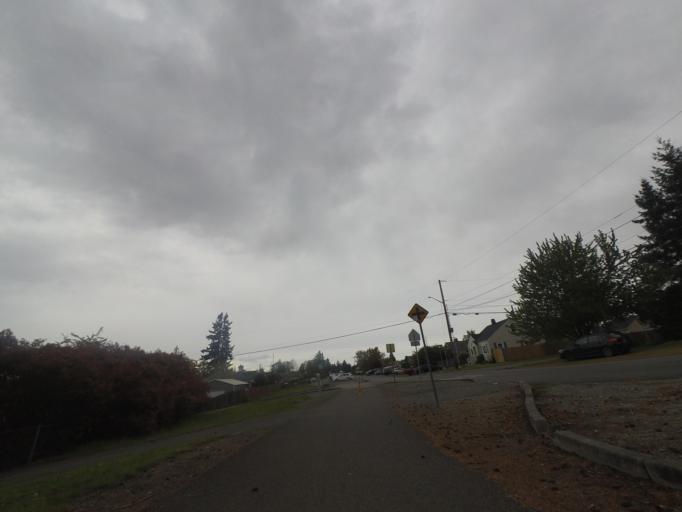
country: US
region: Washington
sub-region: Pierce County
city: Lakewood
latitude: 47.1934
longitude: -122.4757
